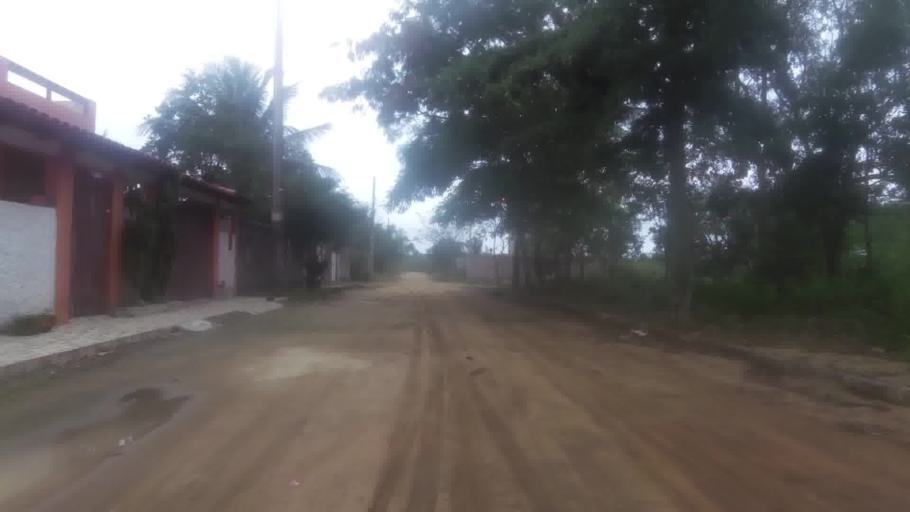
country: BR
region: Espirito Santo
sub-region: Piuma
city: Piuma
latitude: -20.7959
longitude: -40.5877
